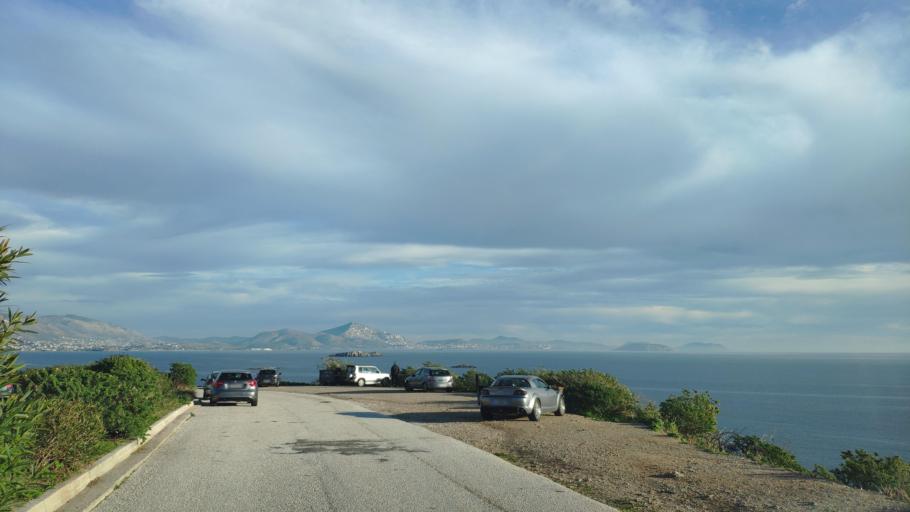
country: GR
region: Attica
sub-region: Nomarchia Anatolikis Attikis
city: Vouliagmeni
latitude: 37.7968
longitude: 23.8002
